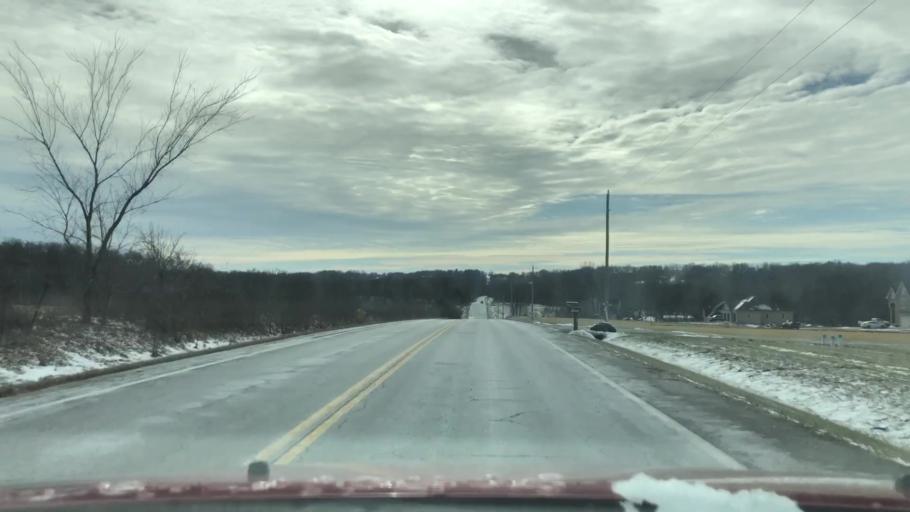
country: US
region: Missouri
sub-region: Jackson County
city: Lone Jack
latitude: 38.9079
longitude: -94.1335
